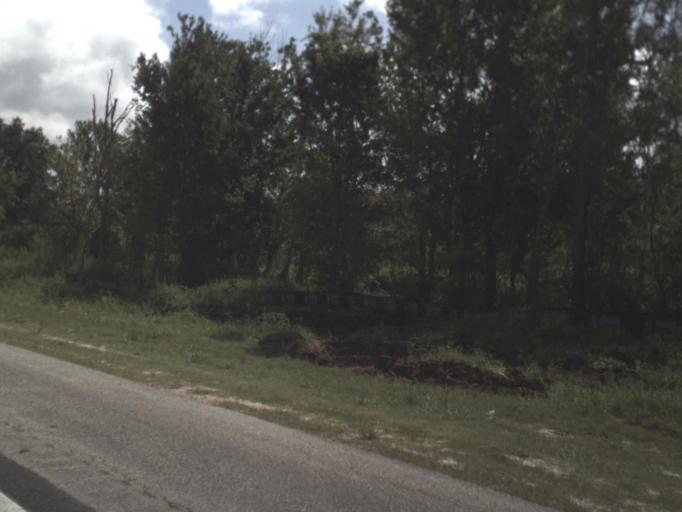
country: US
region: Florida
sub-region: Pasco County
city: Wesley Chapel
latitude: 28.2503
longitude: -82.3441
